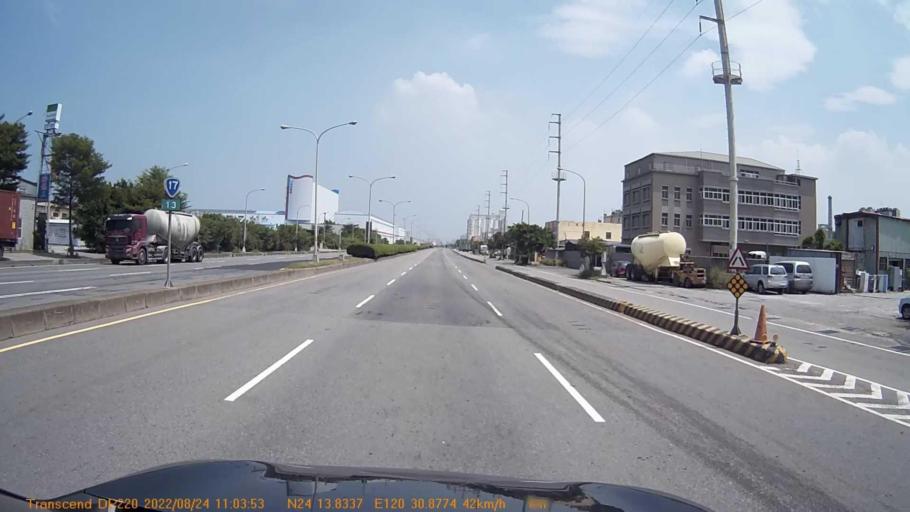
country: TW
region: Taiwan
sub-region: Changhua
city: Chang-hua
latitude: 24.2310
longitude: 120.5148
